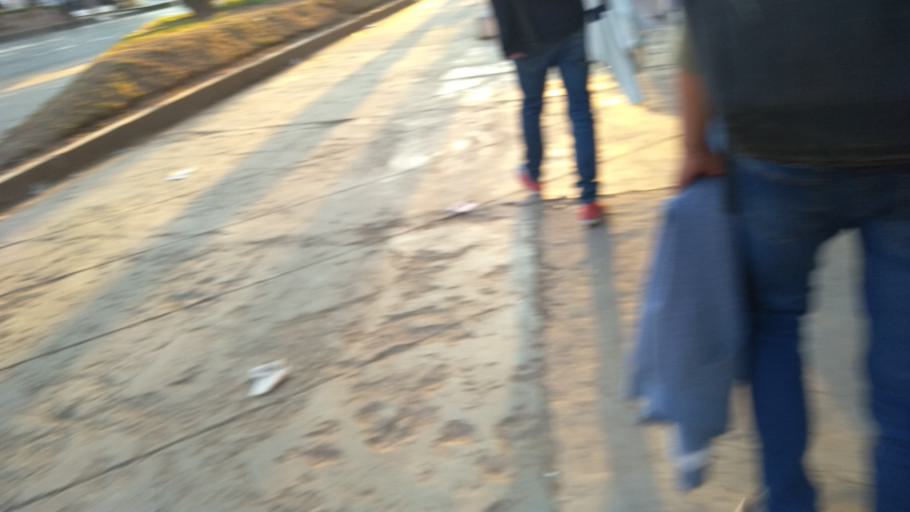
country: PE
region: Cusco
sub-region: Provincia de Cusco
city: Cusco
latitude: -13.5253
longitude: -71.9531
